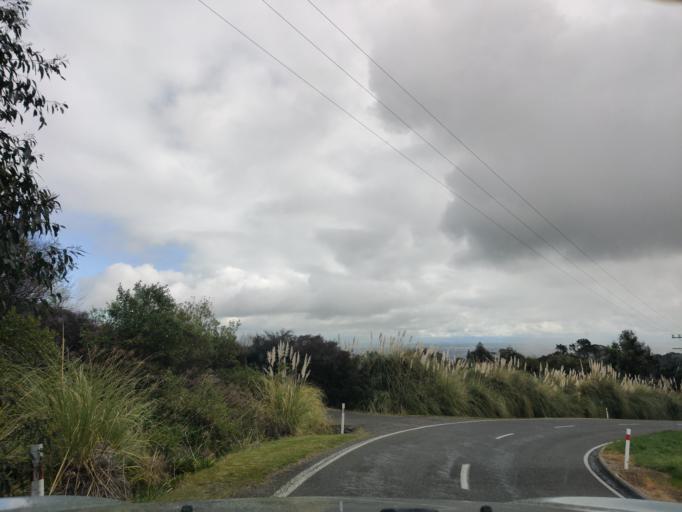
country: NZ
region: Hawke's Bay
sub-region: Hastings District
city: Hastings
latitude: -39.6895
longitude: 176.8997
